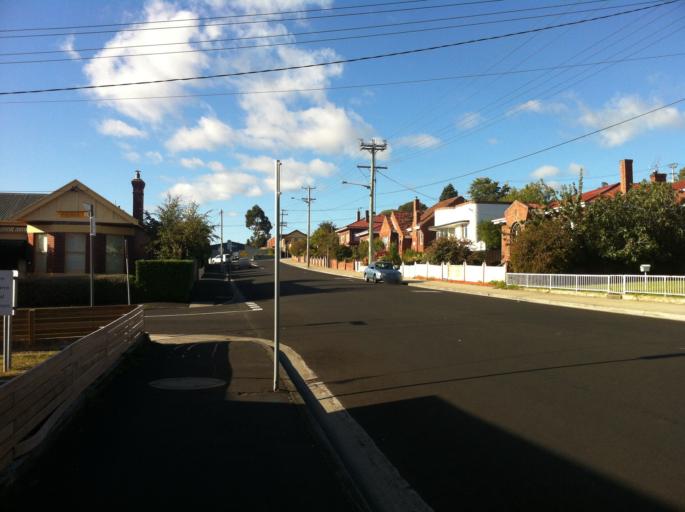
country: AU
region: Tasmania
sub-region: Glenorchy
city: Moonah
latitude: -42.8490
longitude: 147.2948
